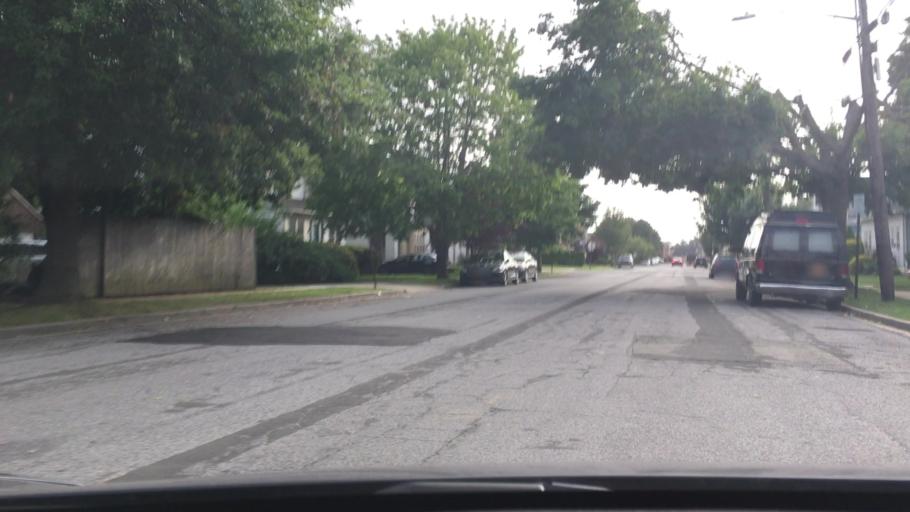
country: US
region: New York
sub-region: Nassau County
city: Hicksville
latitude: 40.7637
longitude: -73.5243
